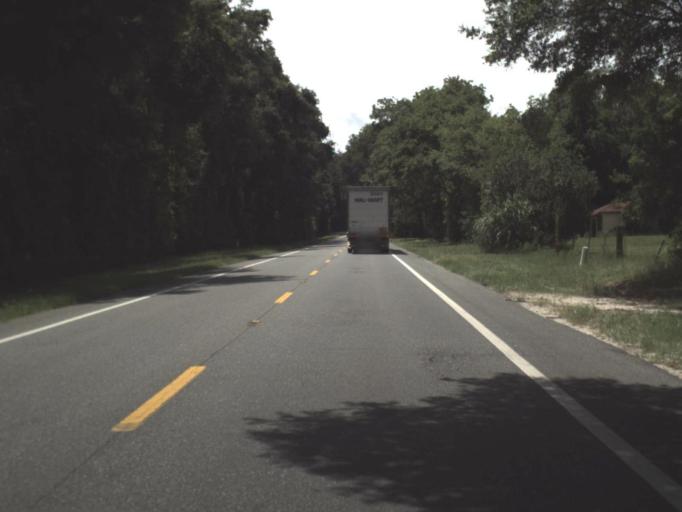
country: US
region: Florida
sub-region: Alachua County
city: Newberry
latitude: 29.5982
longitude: -82.5713
